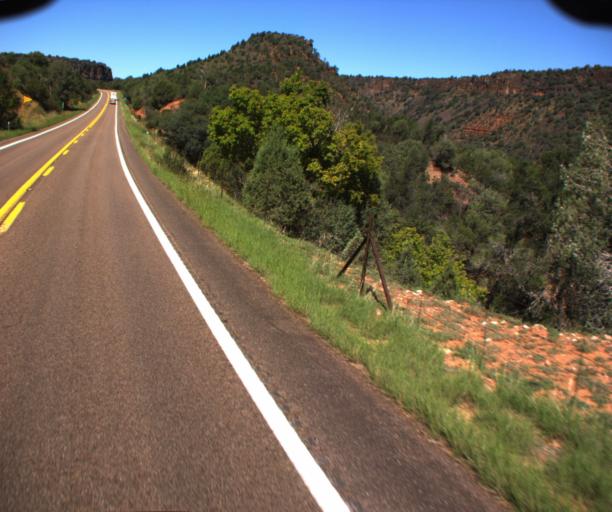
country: US
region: Arizona
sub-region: Navajo County
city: Cibecue
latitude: 34.0128
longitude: -110.2453
